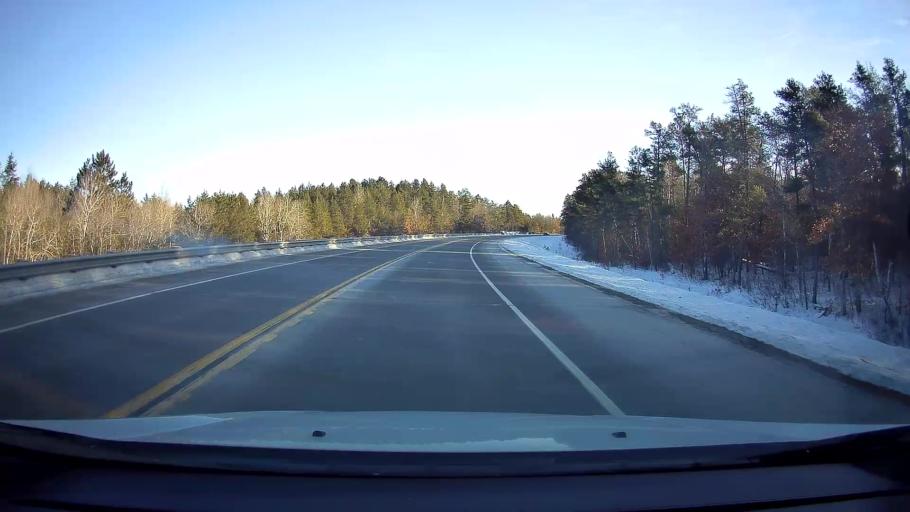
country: US
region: Wisconsin
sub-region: Washburn County
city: Spooner
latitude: 45.9086
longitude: -91.8081
